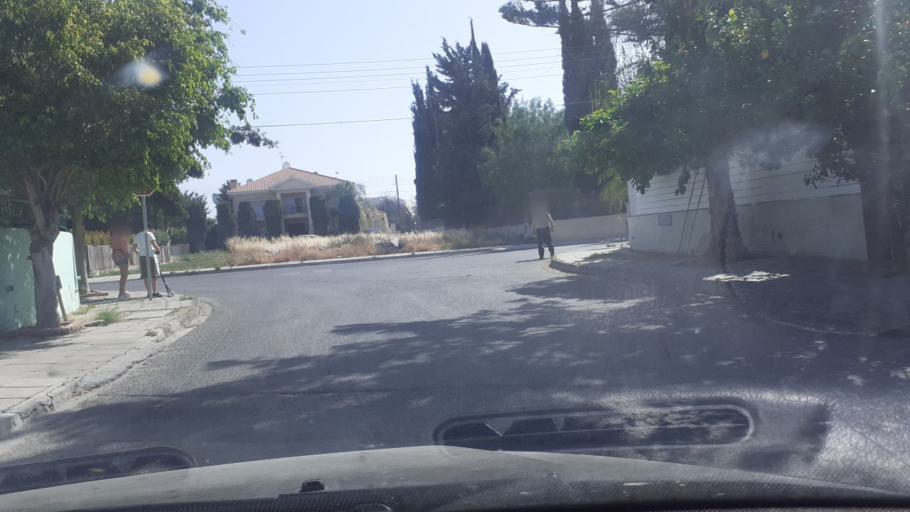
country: CY
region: Limassol
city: Mouttagiaka
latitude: 34.6977
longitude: 33.0734
